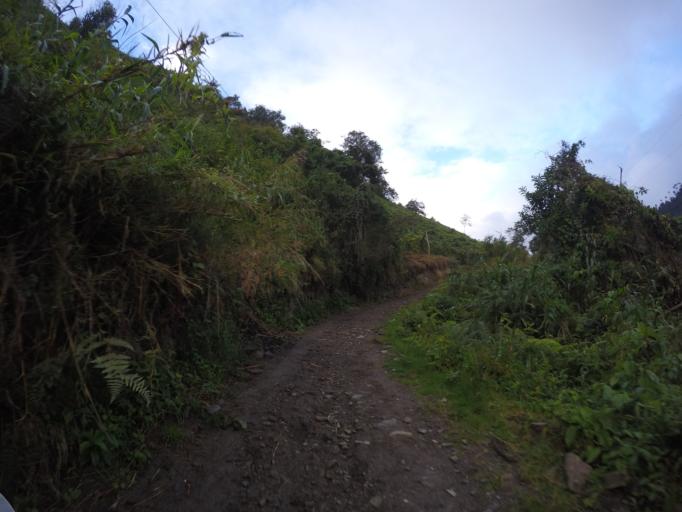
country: CO
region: Tolima
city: Cajamarca
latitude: 4.5070
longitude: -75.3945
